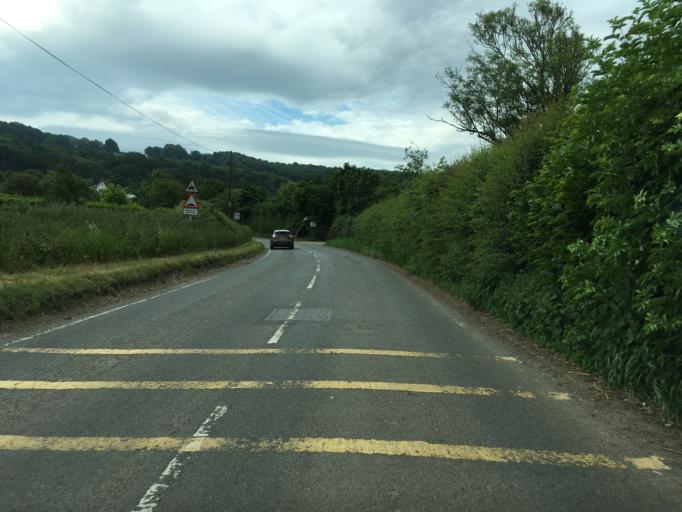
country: GB
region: England
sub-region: North Somerset
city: Portishead
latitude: 51.4658
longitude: -2.7593
